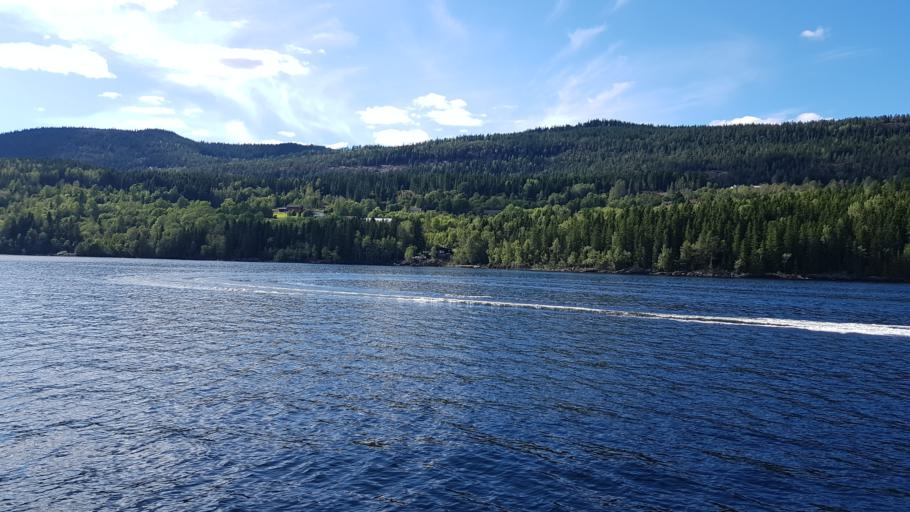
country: NO
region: Akershus
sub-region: Hurdal
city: Hurdal
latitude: 60.5405
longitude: 11.1991
